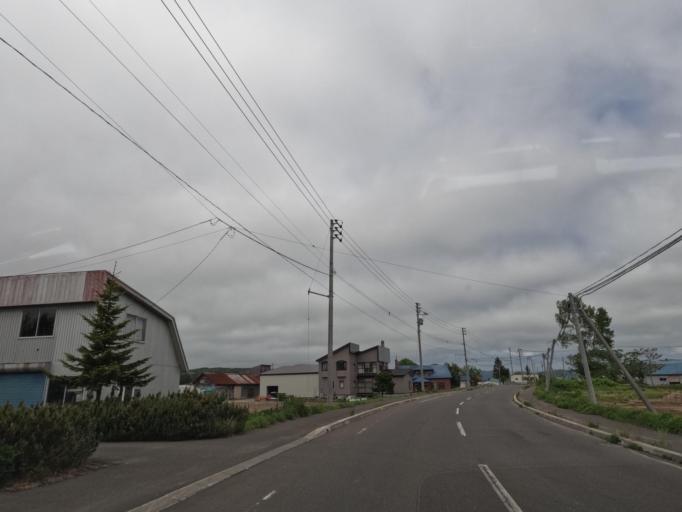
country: JP
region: Hokkaido
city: Tobetsu
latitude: 43.2426
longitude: 141.5139
